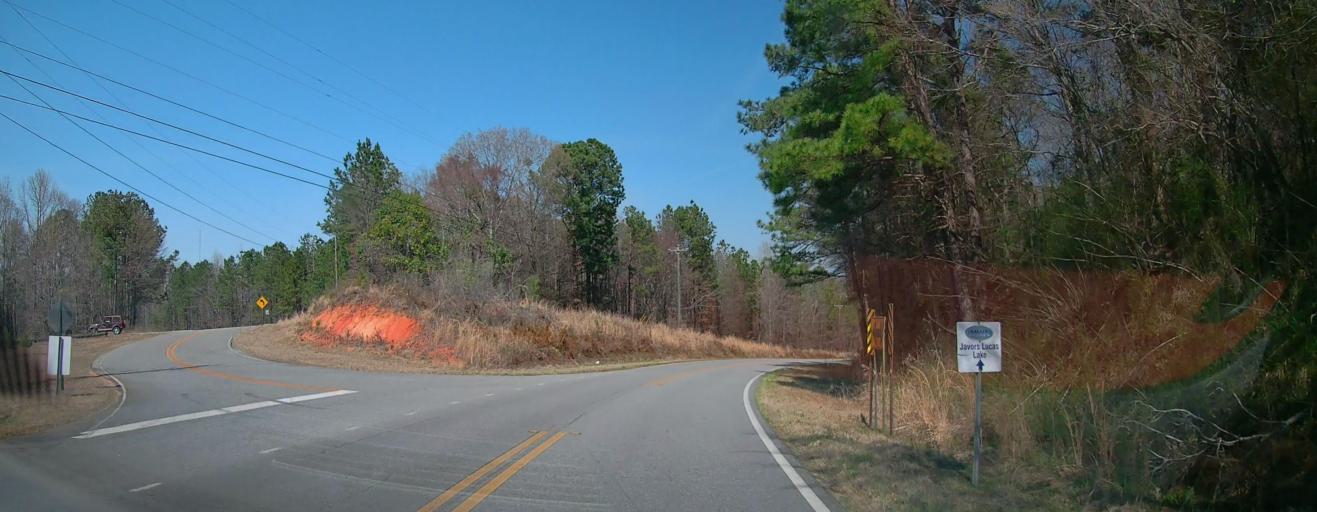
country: US
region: Georgia
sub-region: Bibb County
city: Macon
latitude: 32.8958
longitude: -83.6397
